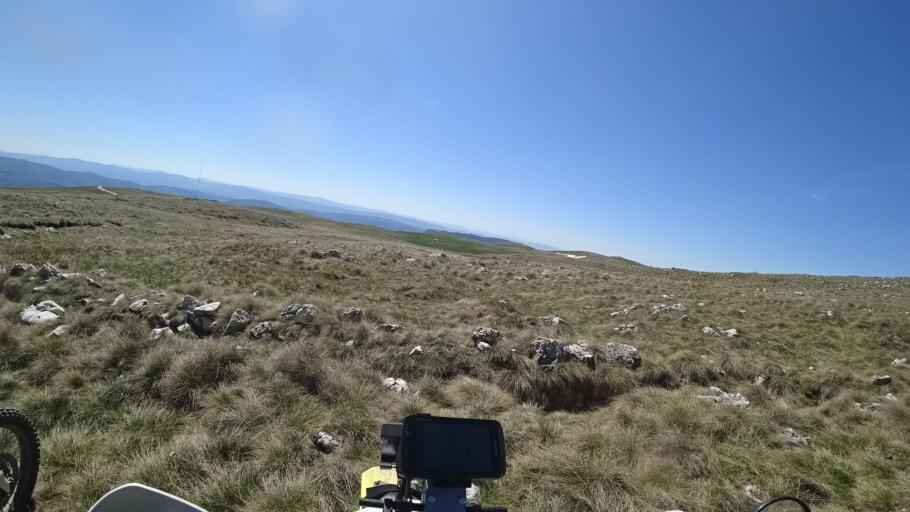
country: BA
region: Federation of Bosnia and Herzegovina
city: Travnik
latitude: 44.2797
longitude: 17.6349
